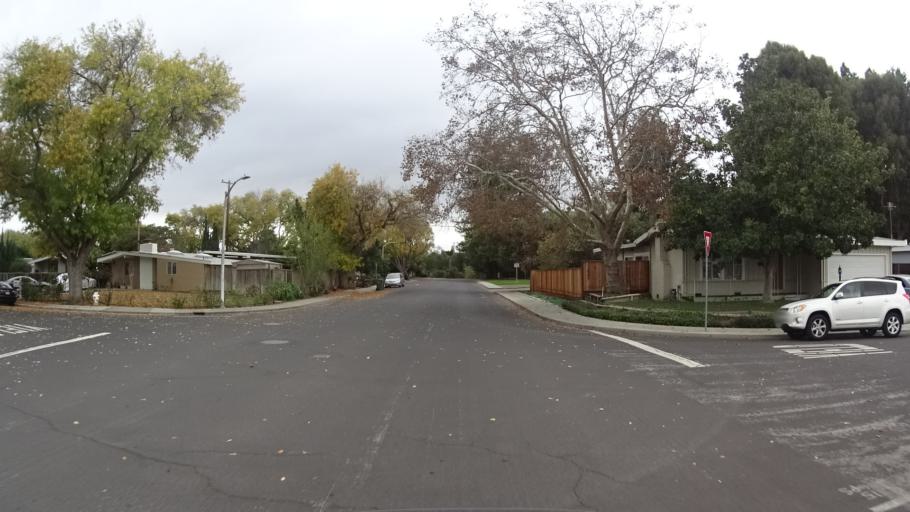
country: US
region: California
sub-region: Santa Clara County
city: Santa Clara
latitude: 37.3351
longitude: -121.9816
